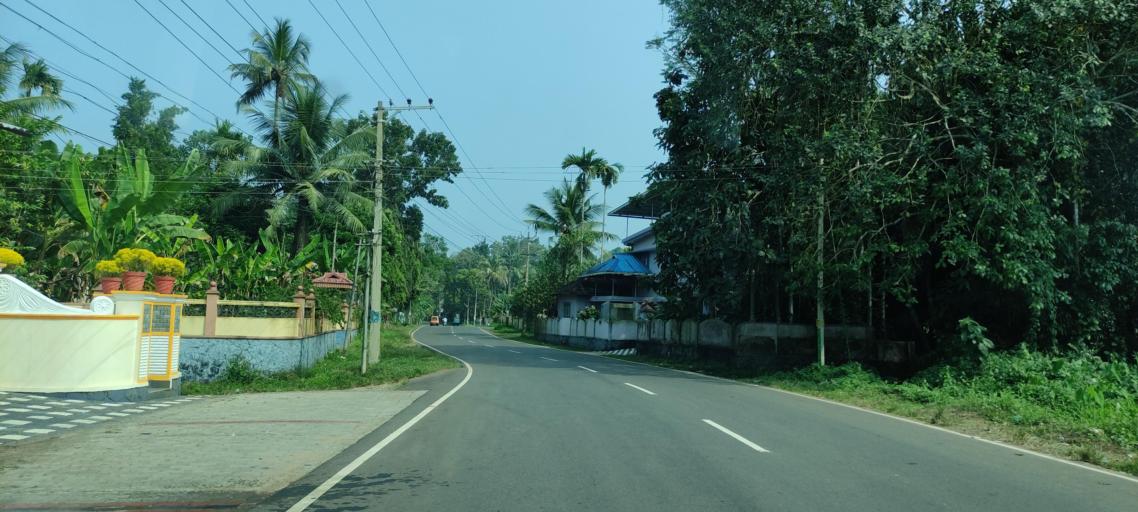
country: IN
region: Kerala
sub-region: Pattanamtitta
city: Adur
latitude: 9.2300
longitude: 76.7118
